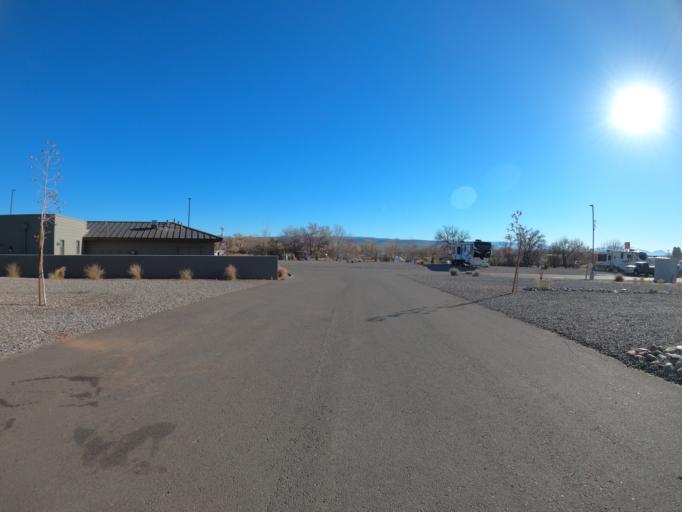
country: US
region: Arizona
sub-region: Yavapai County
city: Camp Verde
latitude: 34.5854
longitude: -111.8831
